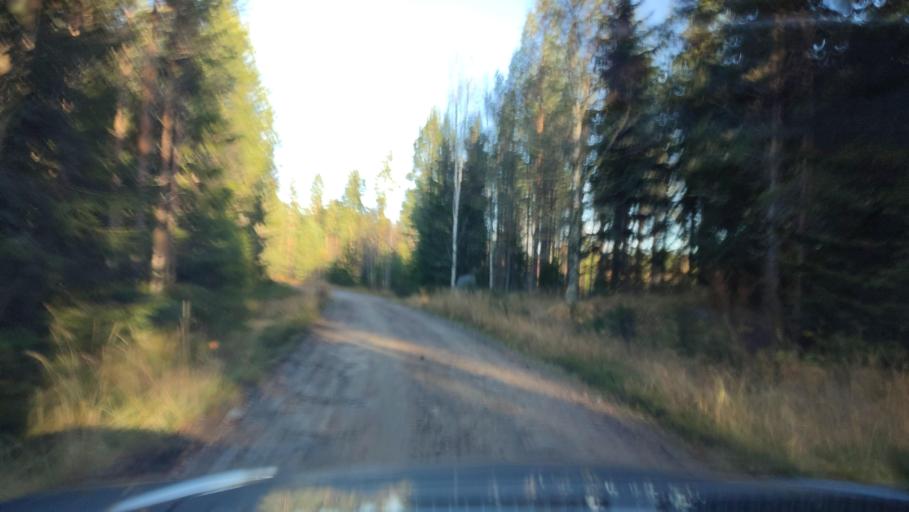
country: FI
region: Southern Ostrobothnia
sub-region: Suupohja
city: Karijoki
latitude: 62.2151
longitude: 21.6277
